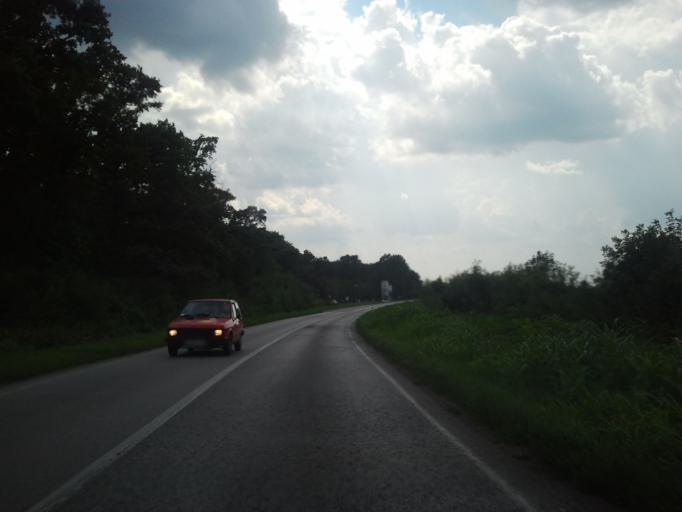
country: RS
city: Celarevo
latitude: 45.2546
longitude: 19.4911
